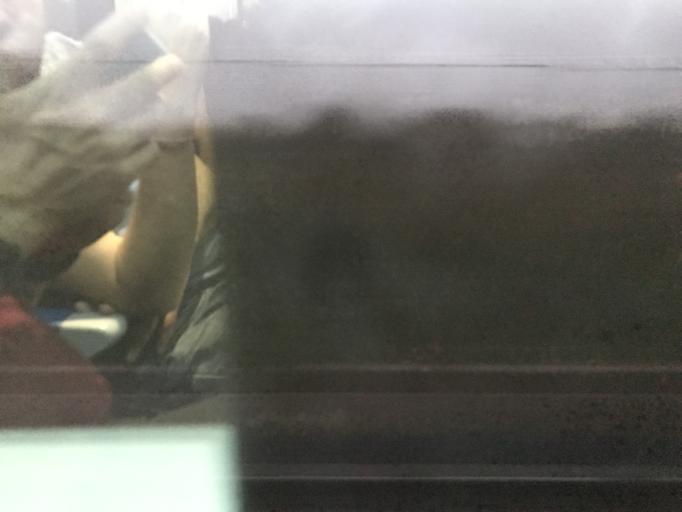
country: TR
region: Kocaeli
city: Derince
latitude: 40.7505
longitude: 29.8125
